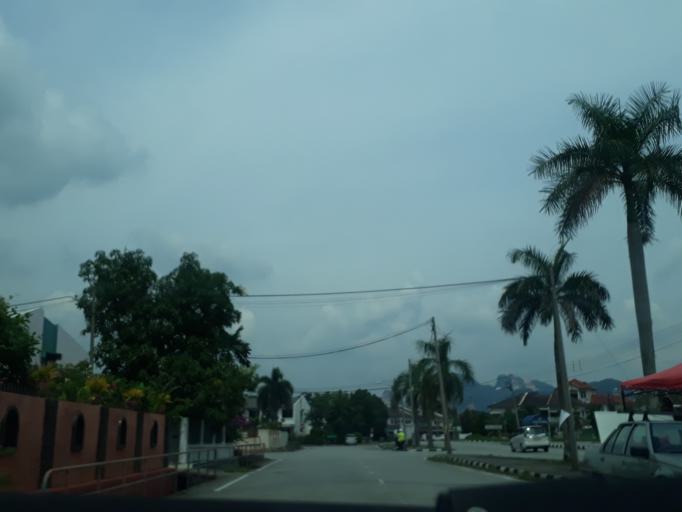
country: MY
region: Perak
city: Ipoh
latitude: 4.5919
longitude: 101.1319
